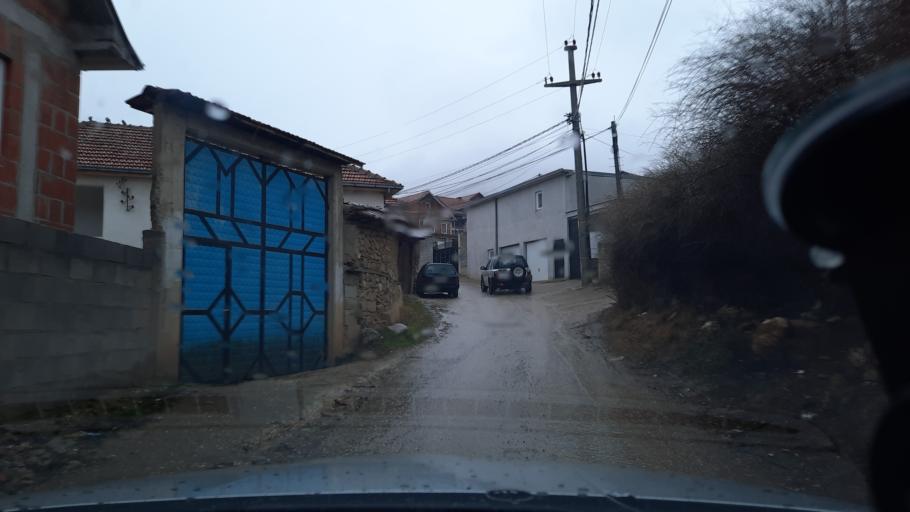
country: MK
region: Opstina Lipkovo
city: Otlja
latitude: 42.1454
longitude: 21.5809
